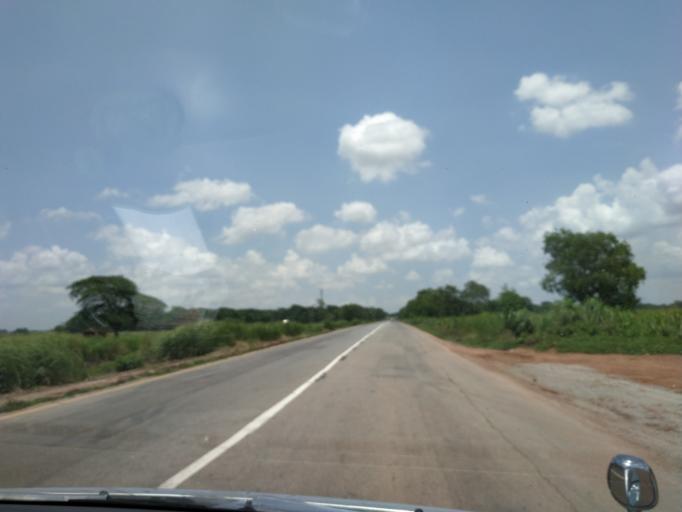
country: MM
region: Bago
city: Thanatpin
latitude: 17.4512
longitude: 96.6181
